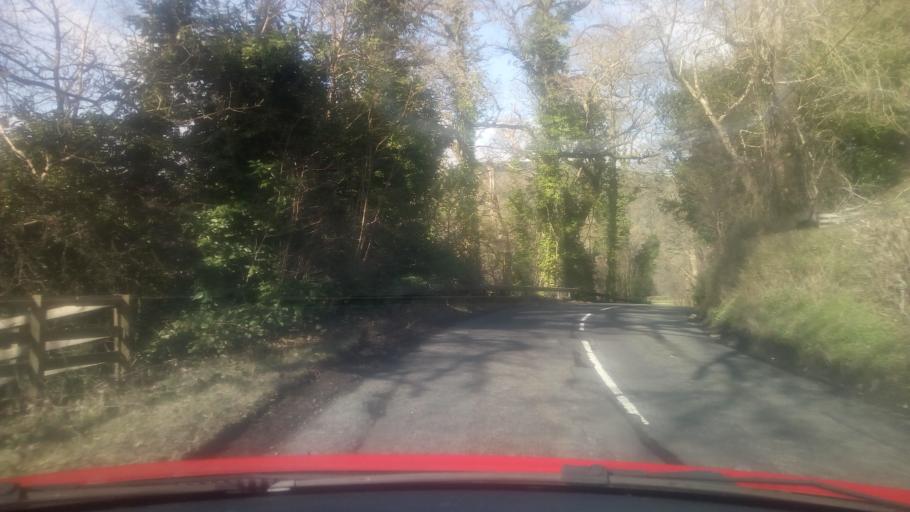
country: GB
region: Scotland
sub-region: The Scottish Borders
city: Selkirk
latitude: 55.5855
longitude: -2.8646
